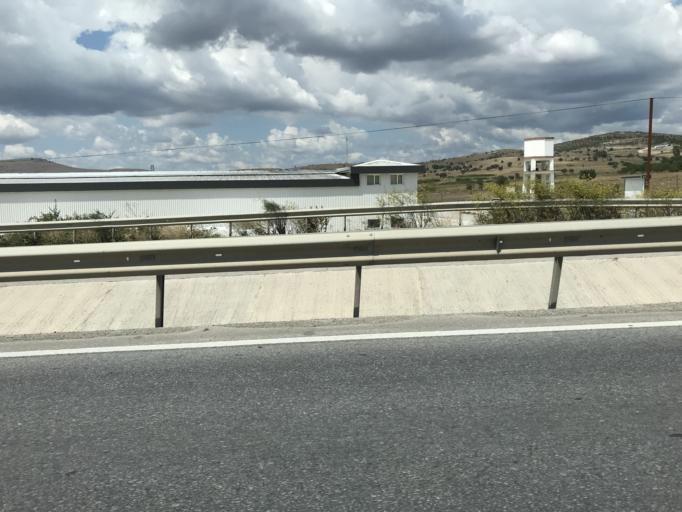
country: TR
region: Balikesir
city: Yenikoy
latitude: 39.7328
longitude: 27.9763
